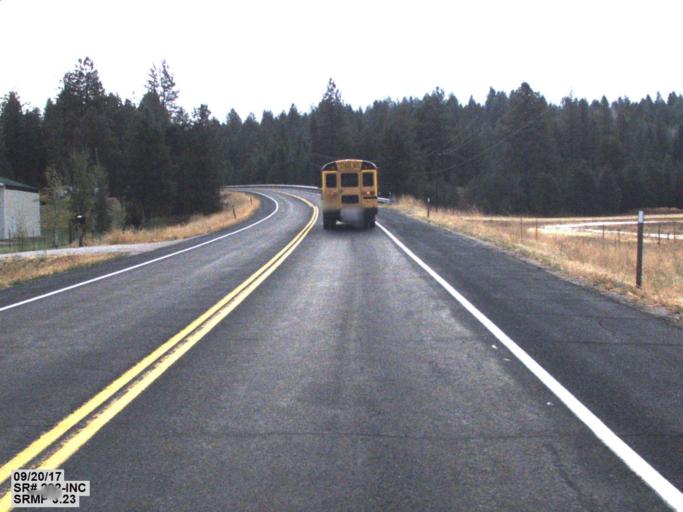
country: US
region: Washington
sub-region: Stevens County
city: Chewelah
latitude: 48.0626
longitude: -117.6758
